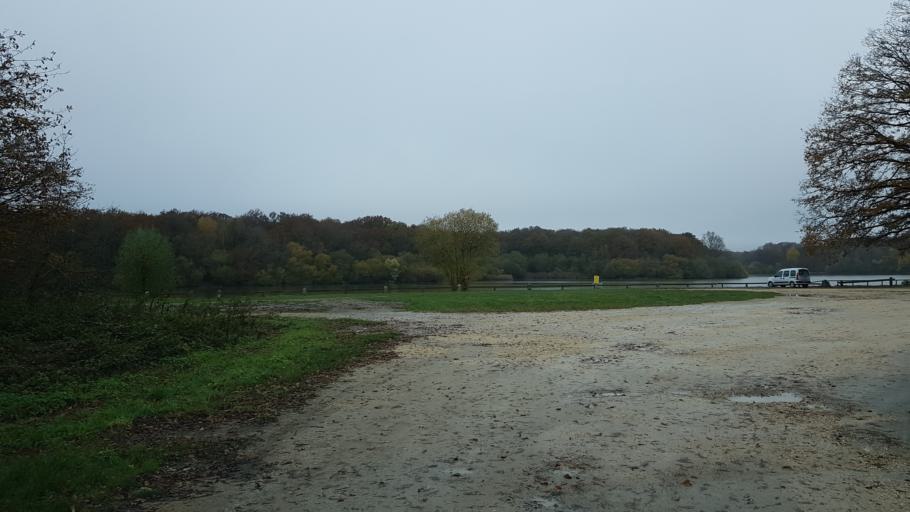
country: FR
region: Ile-de-France
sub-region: Departement des Yvelines
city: Auffargis
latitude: 48.6544
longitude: 1.8859
